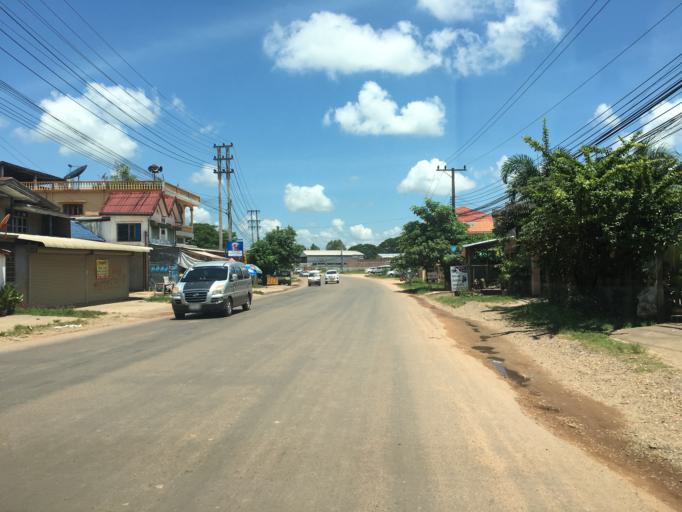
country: LA
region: Vientiane
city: Vientiane
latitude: 18.0487
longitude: 102.5454
